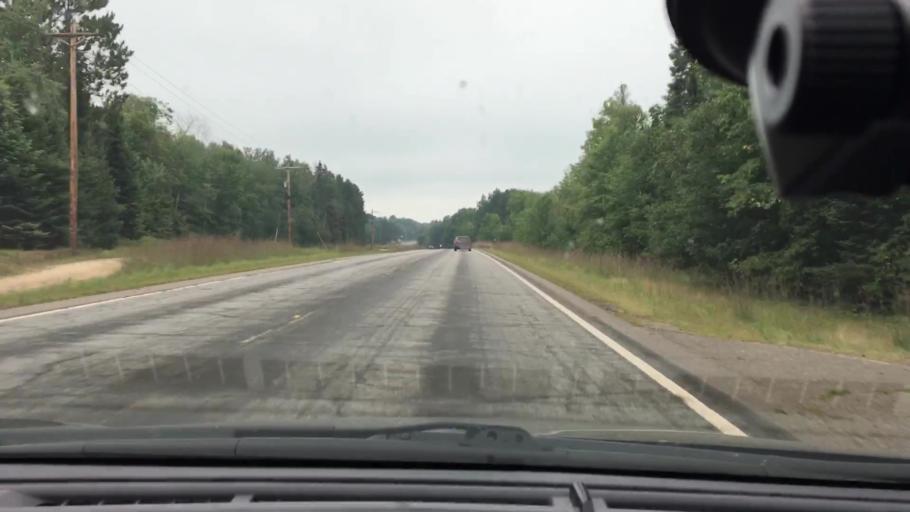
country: US
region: Minnesota
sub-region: Crow Wing County
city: Cross Lake
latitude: 46.8115
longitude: -93.9480
